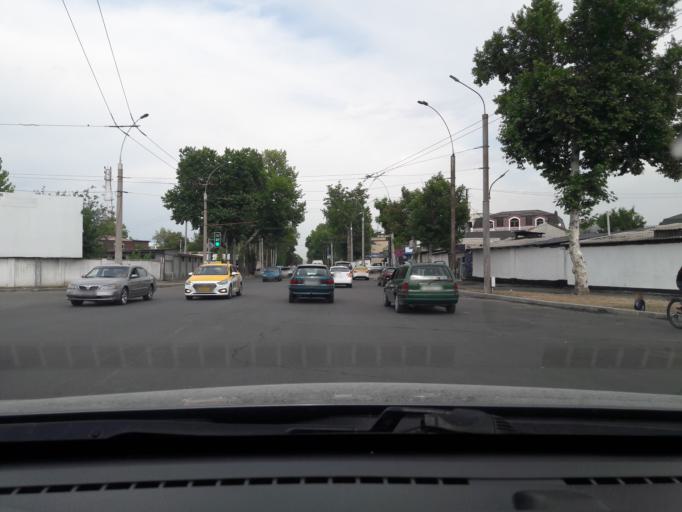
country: TJ
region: Dushanbe
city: Dushanbe
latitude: 38.5461
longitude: 68.7497
